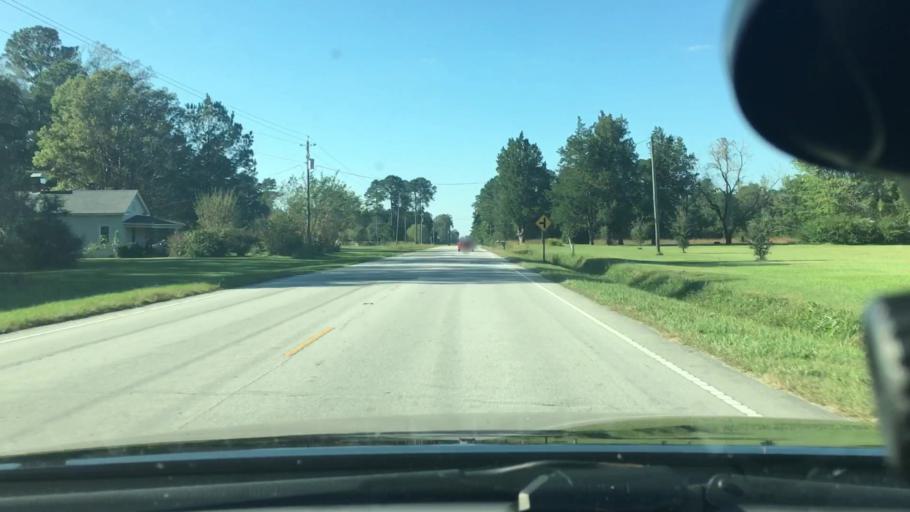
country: US
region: North Carolina
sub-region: Craven County
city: Vanceboro
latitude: 35.3565
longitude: -77.1933
